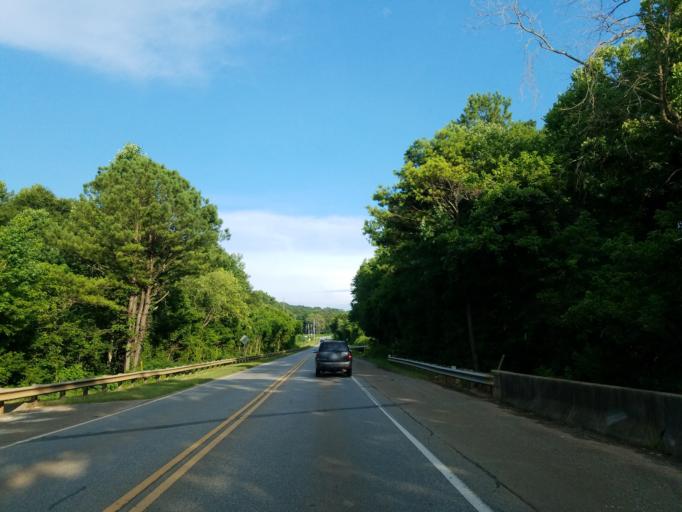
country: US
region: Georgia
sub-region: Bartow County
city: Emerson
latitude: 34.1463
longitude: -84.7708
